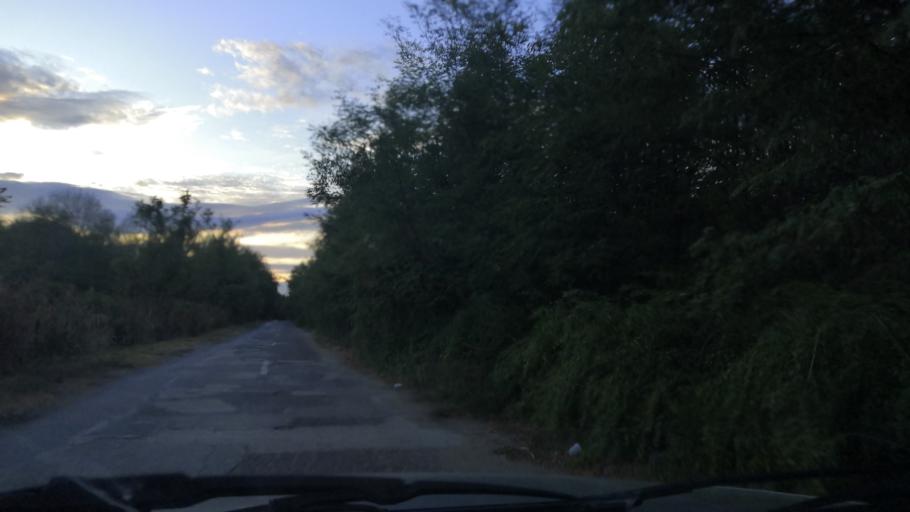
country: RO
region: Mehedinti
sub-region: Comuna Gruia
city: Izvoarele
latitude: 44.2819
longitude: 22.6419
